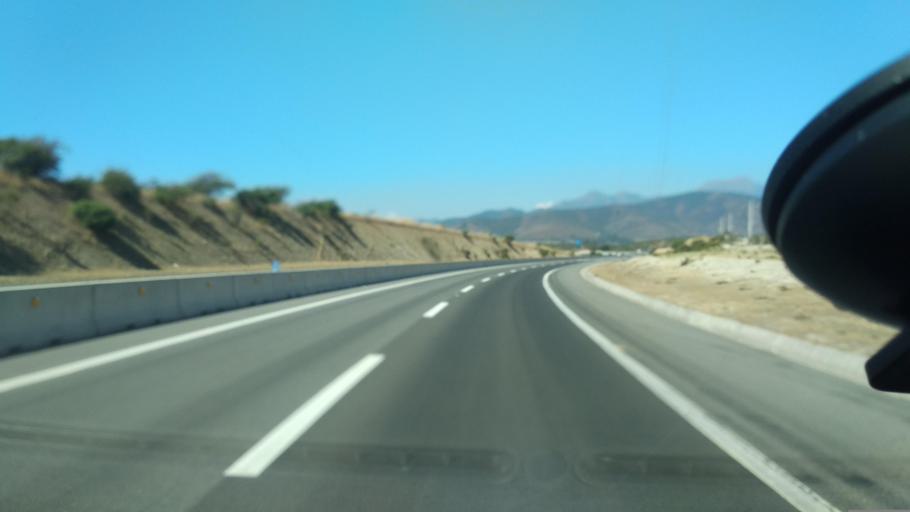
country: CL
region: Valparaiso
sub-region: Provincia de Marga Marga
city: Limache
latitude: -32.9878
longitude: -71.3251
